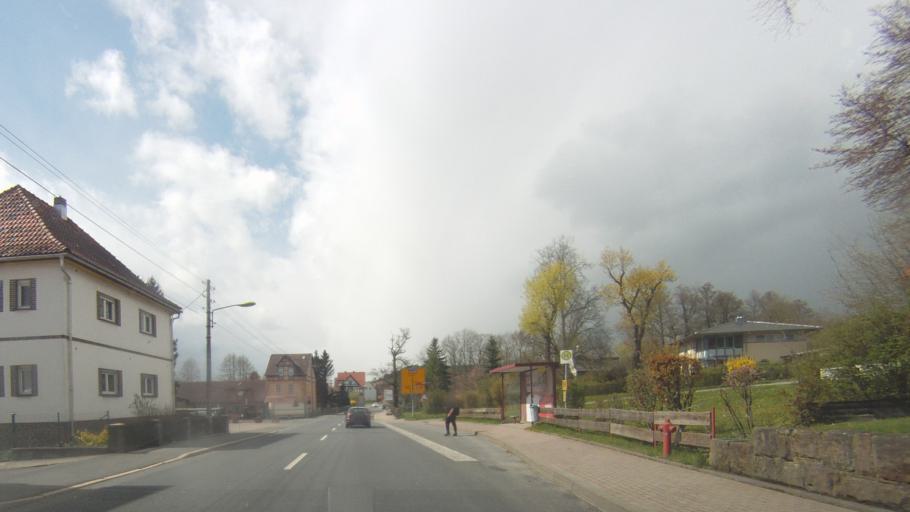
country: DE
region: Thuringia
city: Schalkau
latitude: 50.3979
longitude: 11.0043
